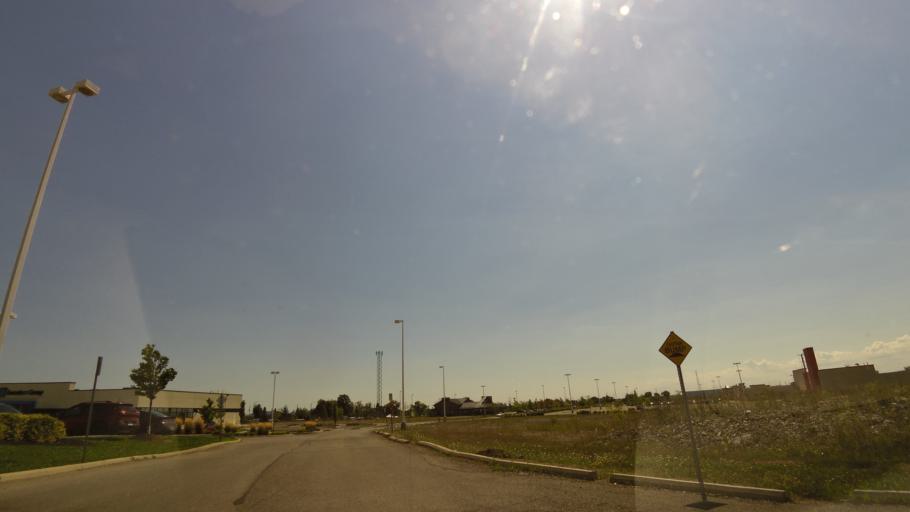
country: CA
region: Ontario
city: Hamilton
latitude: 43.3191
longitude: -79.9153
